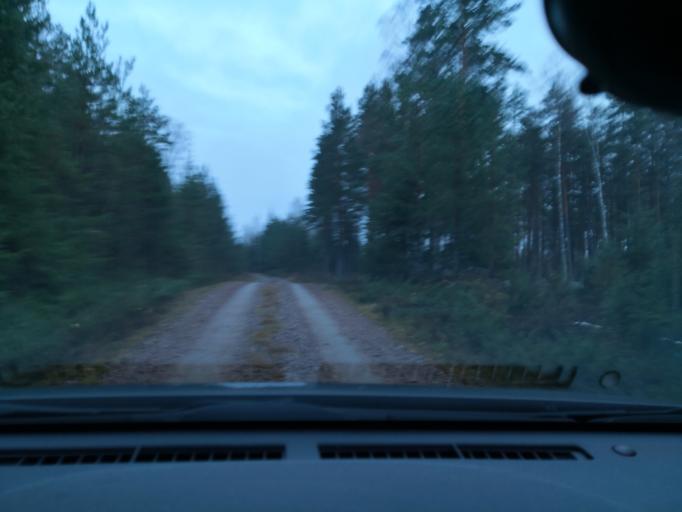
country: SE
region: Vaestmanland
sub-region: Hallstahammars Kommun
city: Kolback
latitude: 59.5515
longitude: 16.1669
